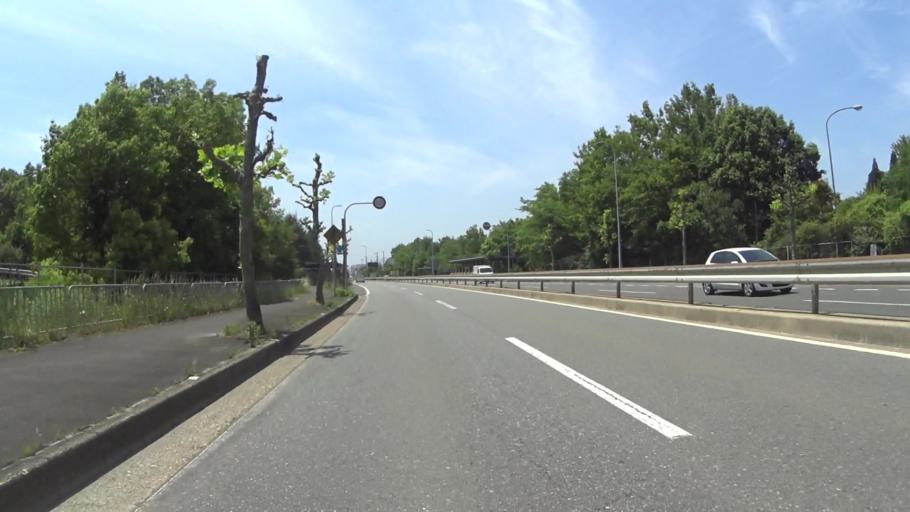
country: JP
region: Kyoto
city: Fukuchiyama
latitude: 35.2828
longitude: 135.1781
